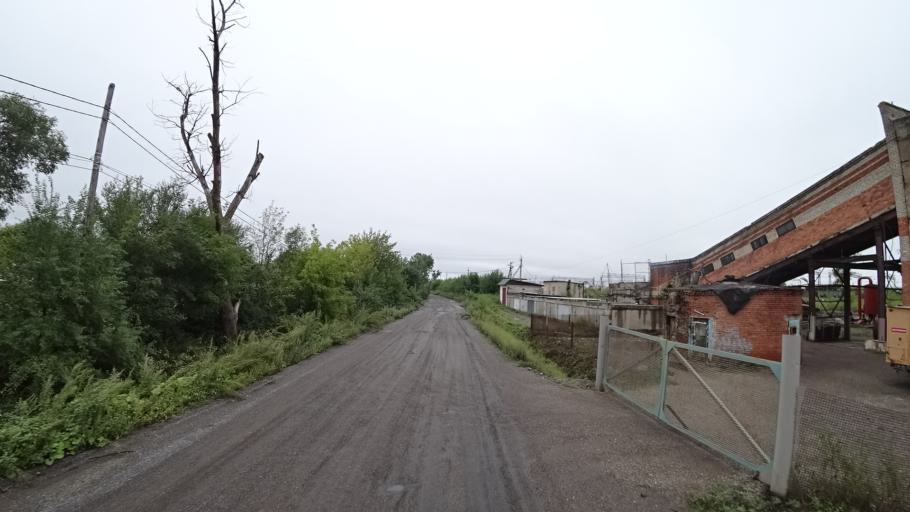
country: RU
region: Primorskiy
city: Monastyrishche
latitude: 44.2104
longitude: 132.4433
